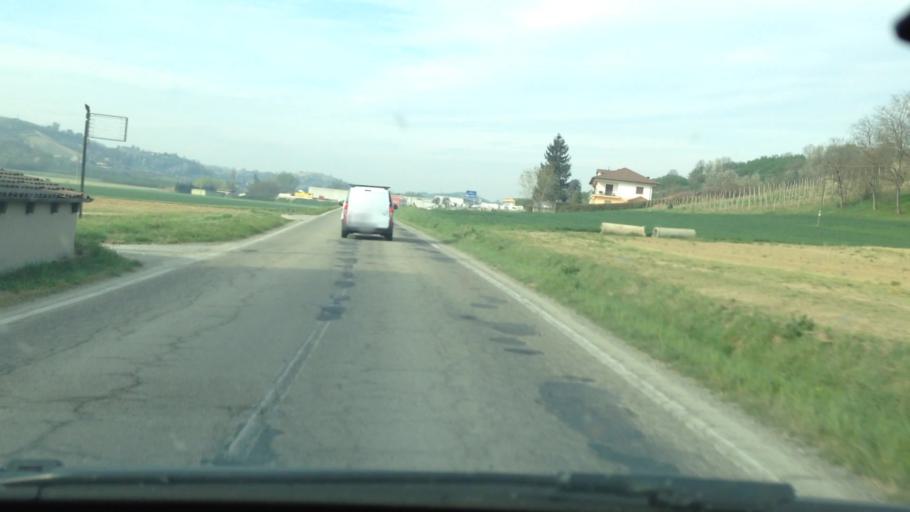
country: IT
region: Piedmont
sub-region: Provincia di Asti
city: San Damiano d'Asti
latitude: 44.8100
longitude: 8.0376
